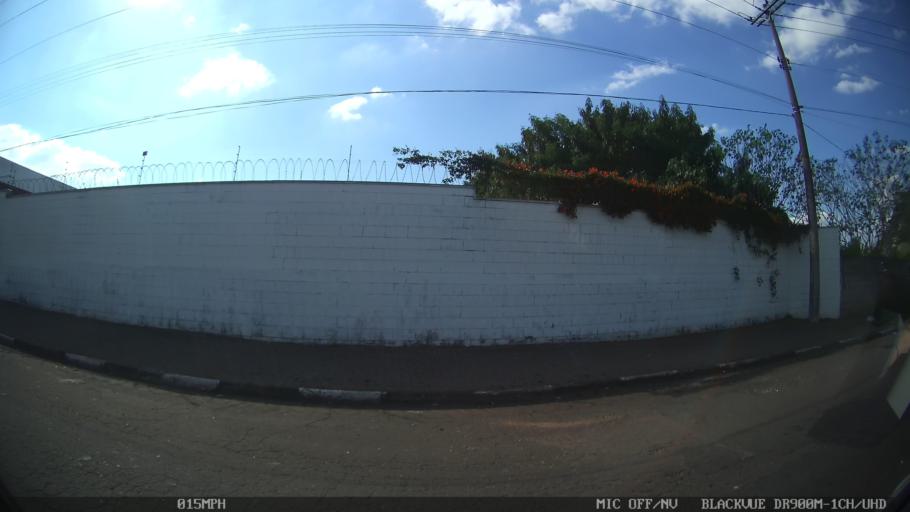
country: BR
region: Sao Paulo
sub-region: Sumare
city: Sumare
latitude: -22.8086
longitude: -47.2816
